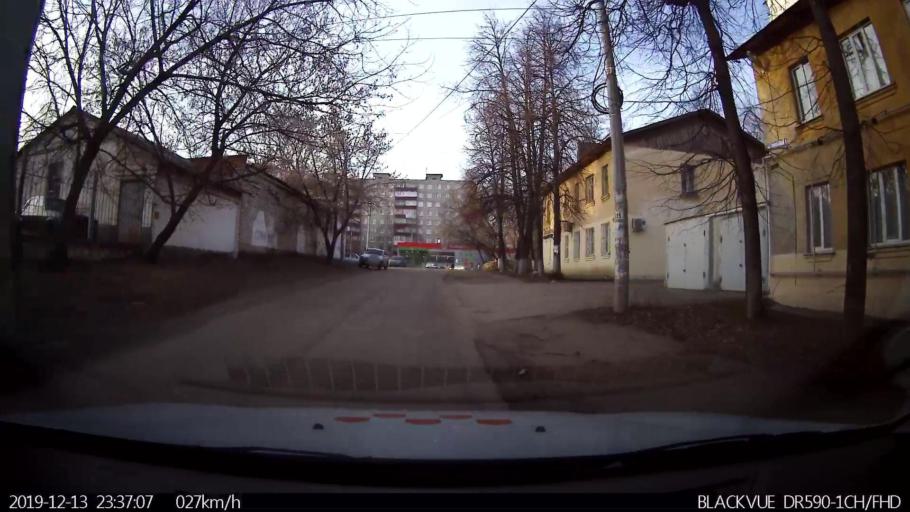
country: RU
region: Nizjnij Novgorod
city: Nizhniy Novgorod
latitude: 56.2932
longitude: 43.9437
